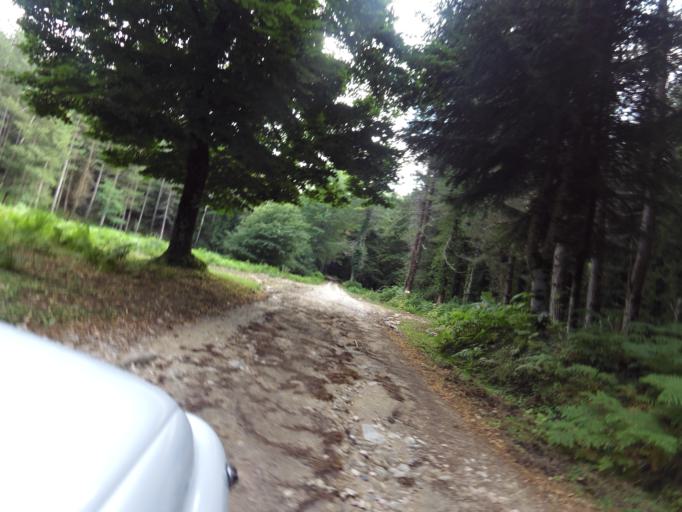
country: IT
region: Calabria
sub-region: Provincia di Vibo-Valentia
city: Nardodipace
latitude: 38.5146
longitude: 16.3789
